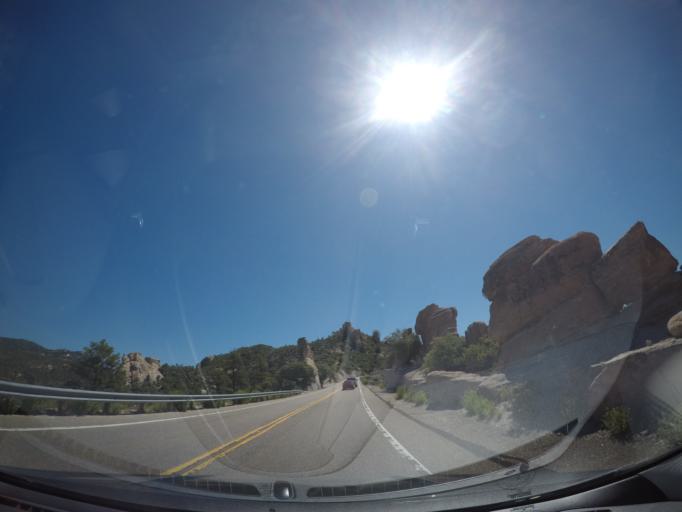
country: US
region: Arizona
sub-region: Pima County
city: Tanque Verde
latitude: 32.3747
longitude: -110.7077
